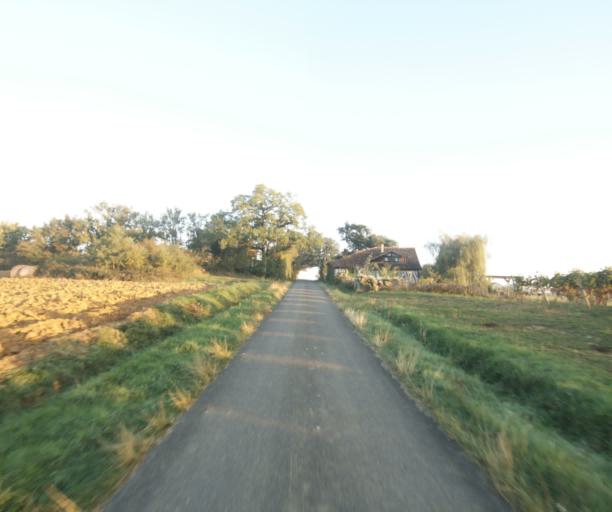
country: FR
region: Midi-Pyrenees
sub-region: Departement du Gers
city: Eauze
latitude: 43.7874
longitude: 0.1694
